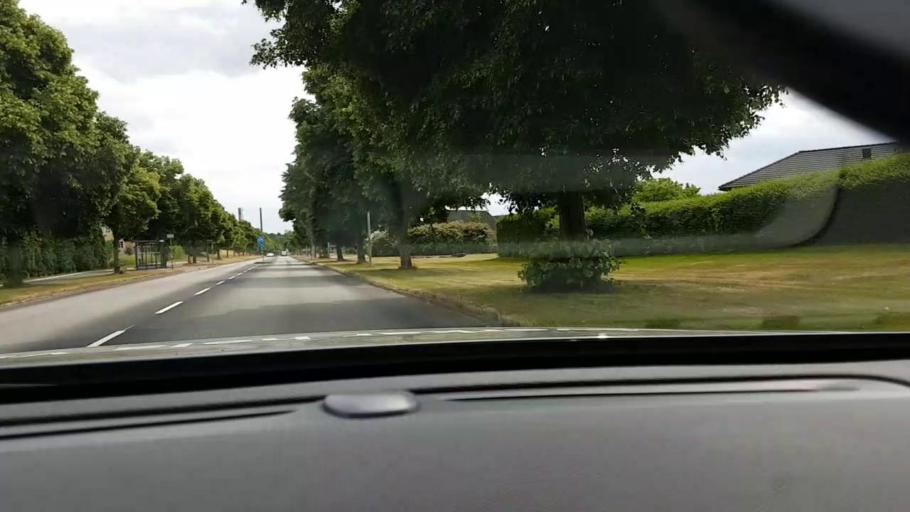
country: SE
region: Skane
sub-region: Hassleholms Kommun
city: Hassleholm
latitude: 56.1711
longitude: 13.7790
